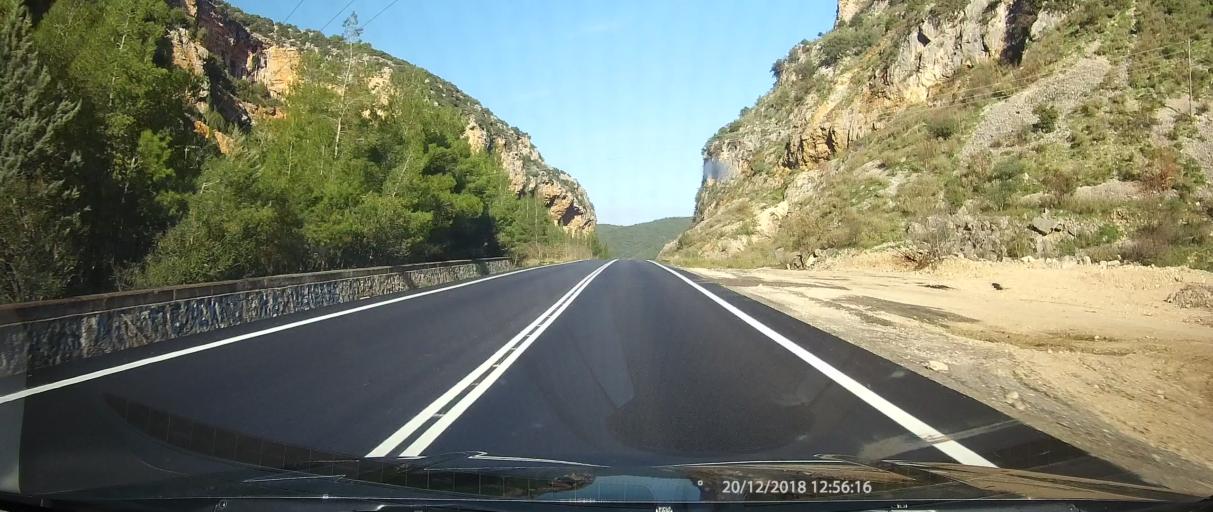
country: GR
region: West Greece
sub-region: Nomos Aitolias kai Akarnanias
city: Pappadhatai
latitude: 38.5079
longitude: 21.3787
